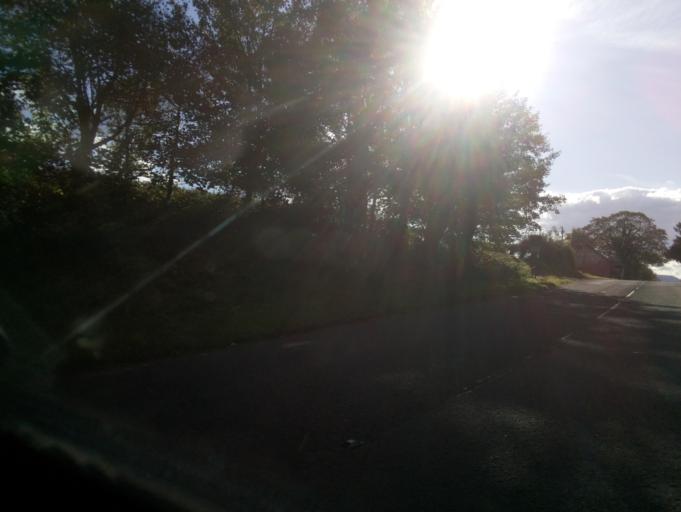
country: GB
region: Wales
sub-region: Sir Powys
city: Brecon
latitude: 51.9634
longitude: -3.3550
